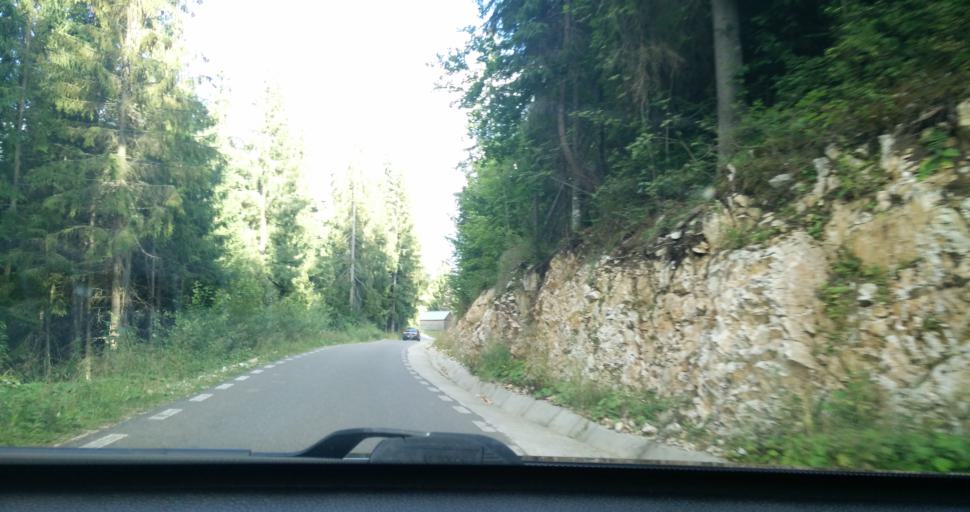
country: RO
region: Alba
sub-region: Comuna Scarisoara
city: Scarisoara
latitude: 46.4860
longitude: 22.8269
